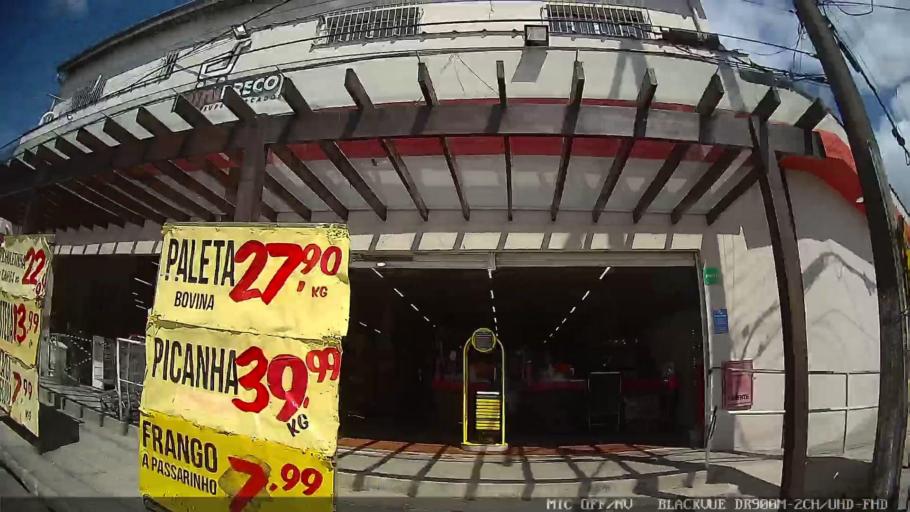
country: BR
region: Sao Paulo
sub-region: Peruibe
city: Peruibe
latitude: -24.3110
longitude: -47.0111
